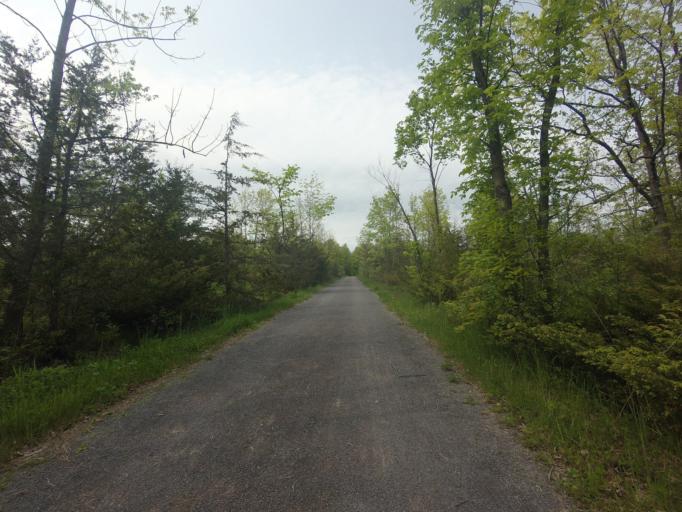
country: CA
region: Ontario
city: Kingston
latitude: 44.3279
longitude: -76.5890
